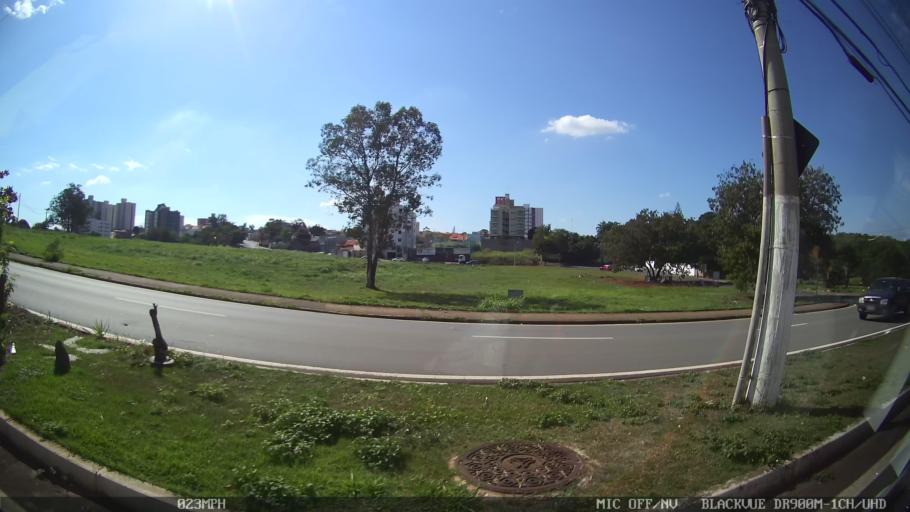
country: BR
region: Sao Paulo
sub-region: Americana
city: Americana
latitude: -22.7442
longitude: -47.3079
